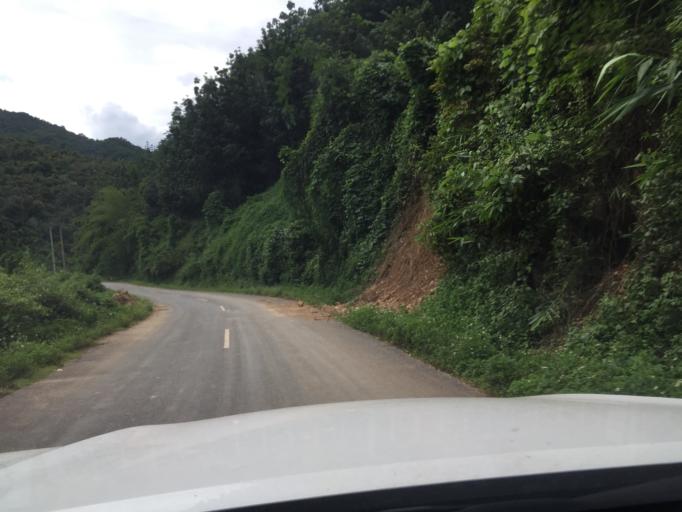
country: LA
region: Oudomxai
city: Muang La
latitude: 21.1038
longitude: 102.2188
